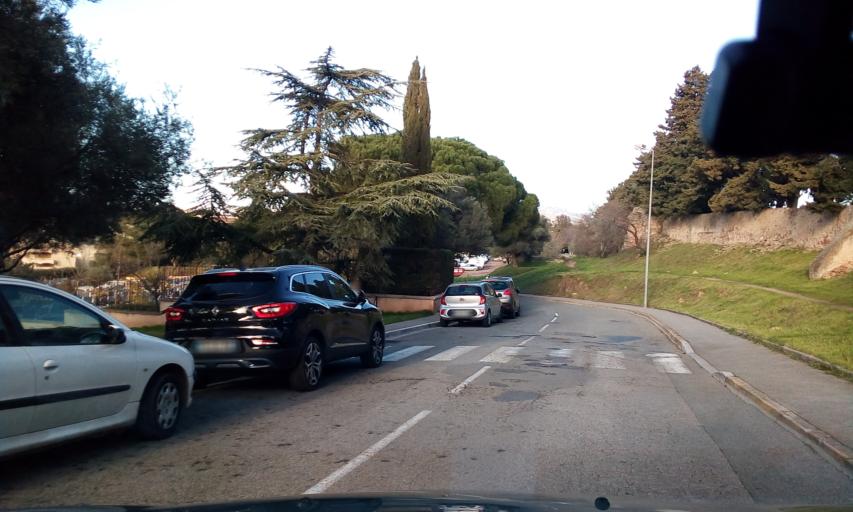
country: FR
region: Provence-Alpes-Cote d'Azur
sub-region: Departement du Var
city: Frejus
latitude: 43.4361
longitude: 6.7346
